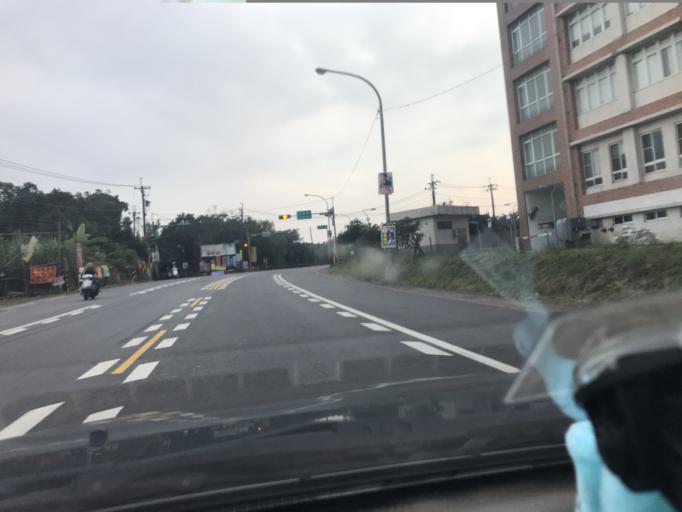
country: TW
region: Taiwan
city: Daxi
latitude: 24.9021
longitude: 121.2306
